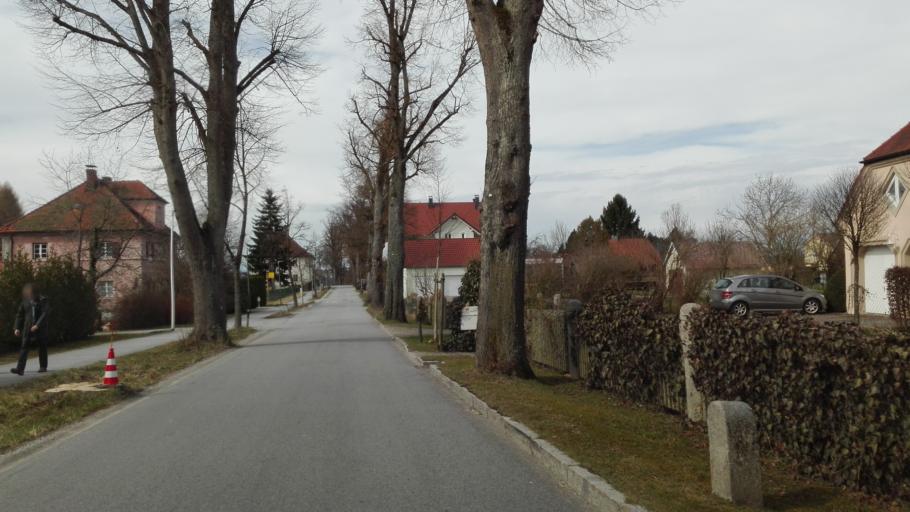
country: DE
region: Bavaria
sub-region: Lower Bavaria
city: Passau
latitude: 48.5582
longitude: 13.4731
